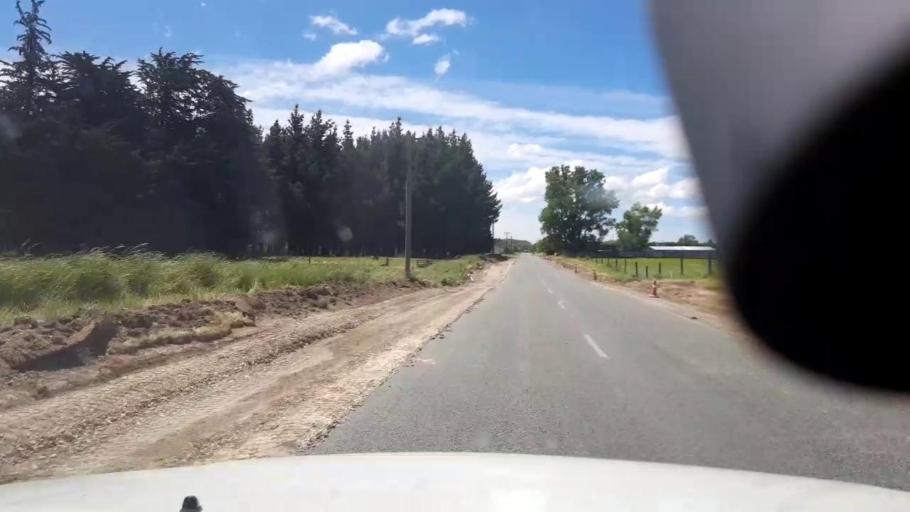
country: NZ
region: Canterbury
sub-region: Timaru District
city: Pleasant Point
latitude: -44.2764
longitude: 171.2507
